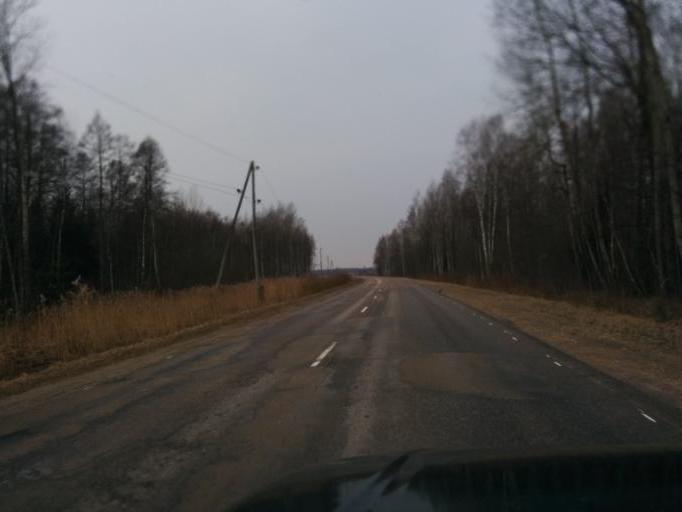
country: LV
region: Ikskile
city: Ikskile
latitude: 56.8150
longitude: 24.4732
